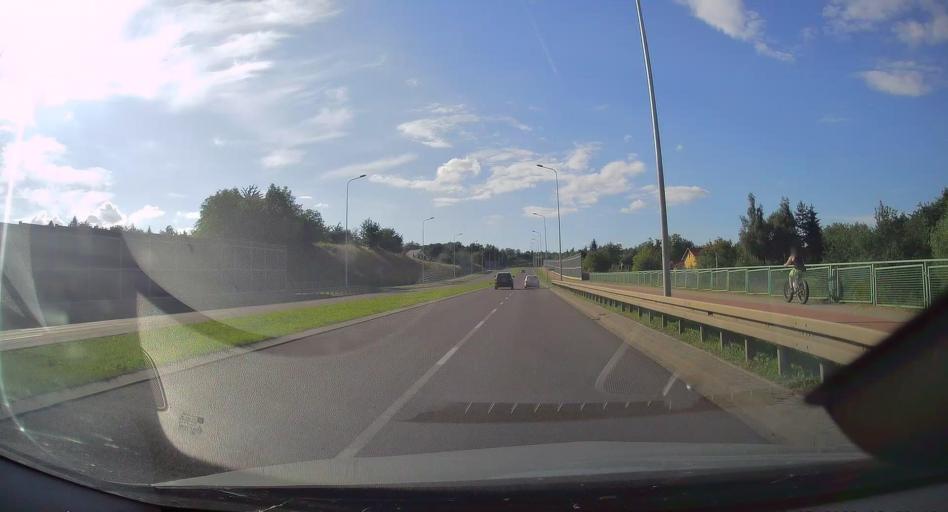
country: PL
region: Subcarpathian Voivodeship
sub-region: Przemysl
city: Przemysl
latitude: 49.8008
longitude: 22.7814
